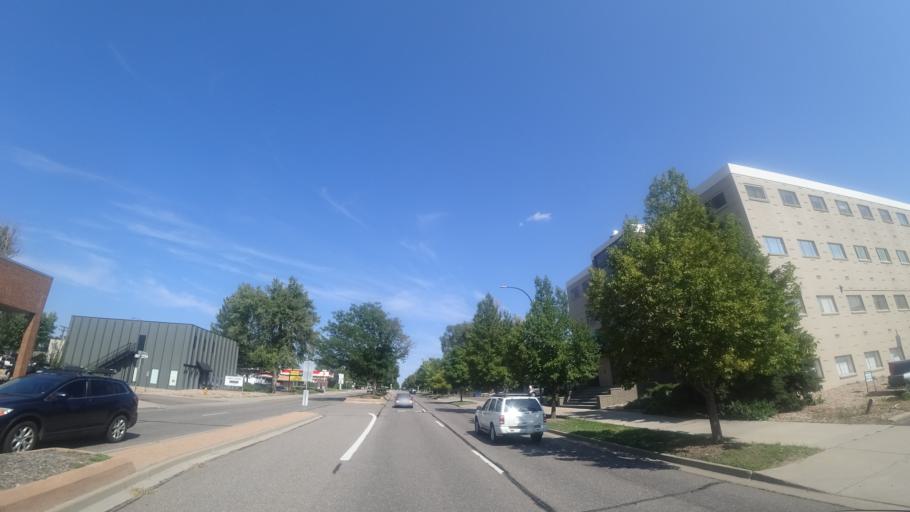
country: US
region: Colorado
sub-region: Arapahoe County
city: Littleton
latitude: 39.6132
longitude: -105.0011
